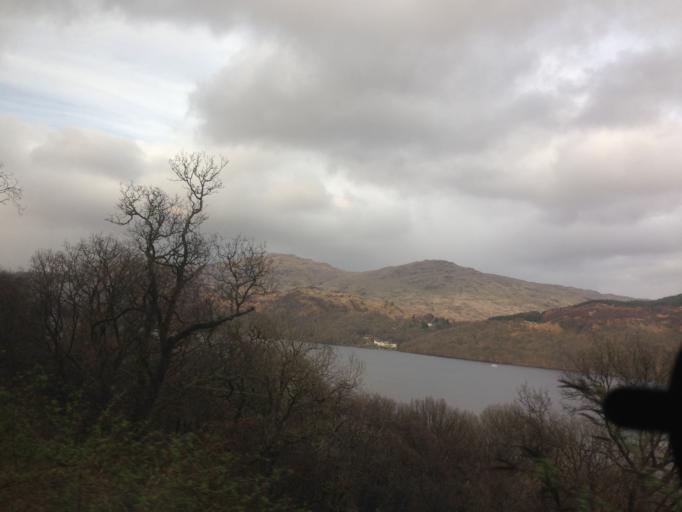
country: GB
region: Scotland
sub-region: Argyll and Bute
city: Garelochhead
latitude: 56.2290
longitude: -4.7020
